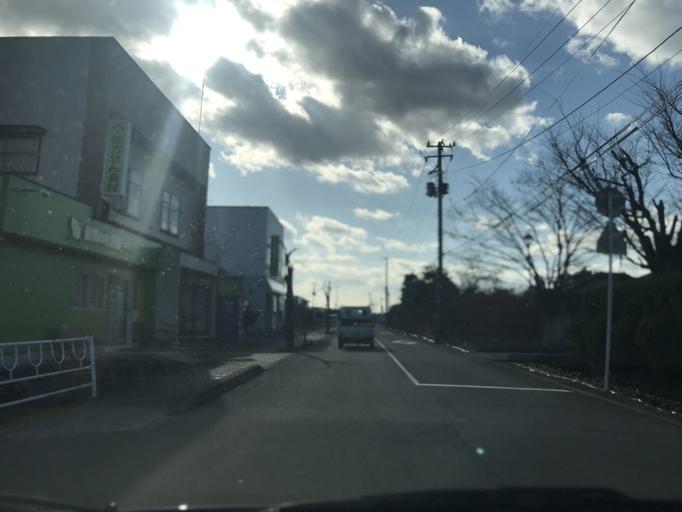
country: JP
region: Iwate
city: Ichinoseki
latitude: 38.7535
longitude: 141.0665
